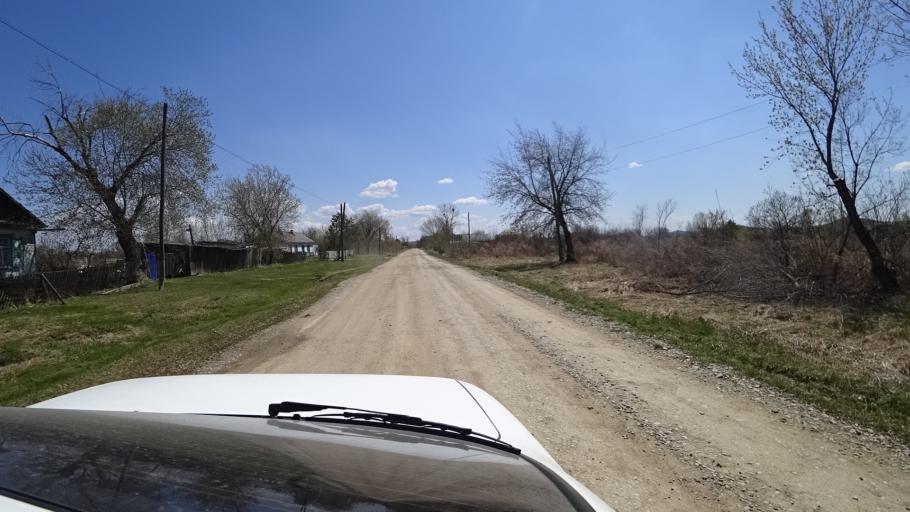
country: RU
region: Primorskiy
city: Dal'nerechensk
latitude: 45.8008
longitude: 133.7657
